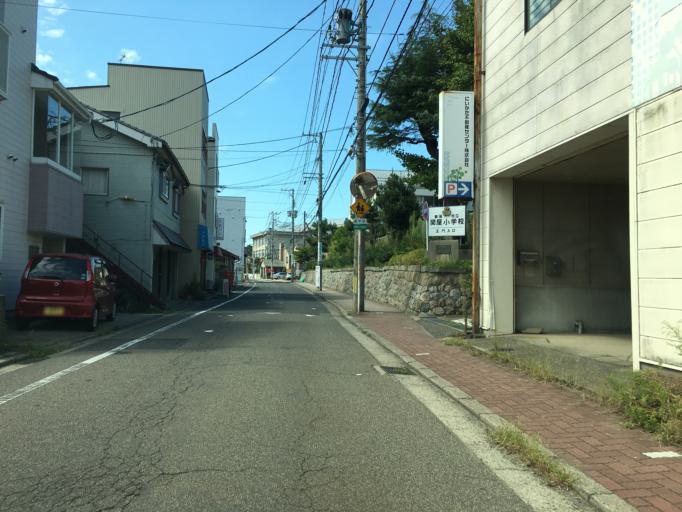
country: JP
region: Niigata
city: Niigata-shi
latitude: 37.9157
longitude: 139.0260
